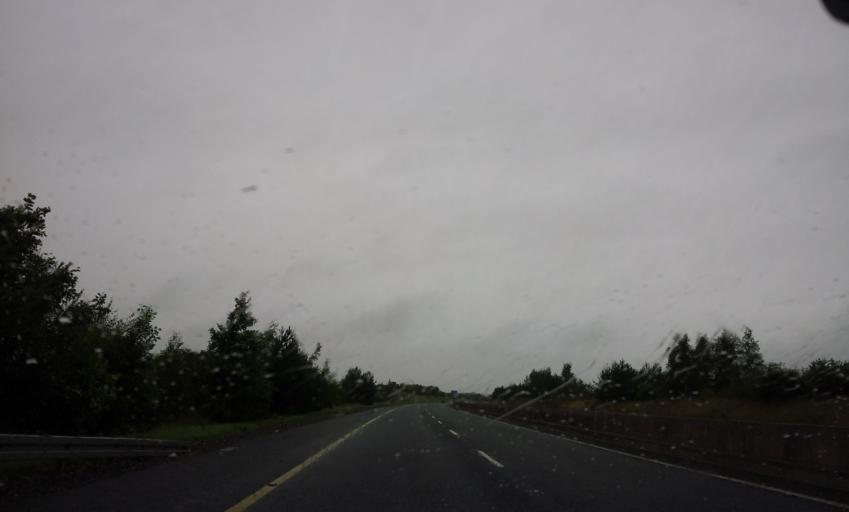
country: IE
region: Munster
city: Cashel
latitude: 52.4734
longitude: -7.9071
